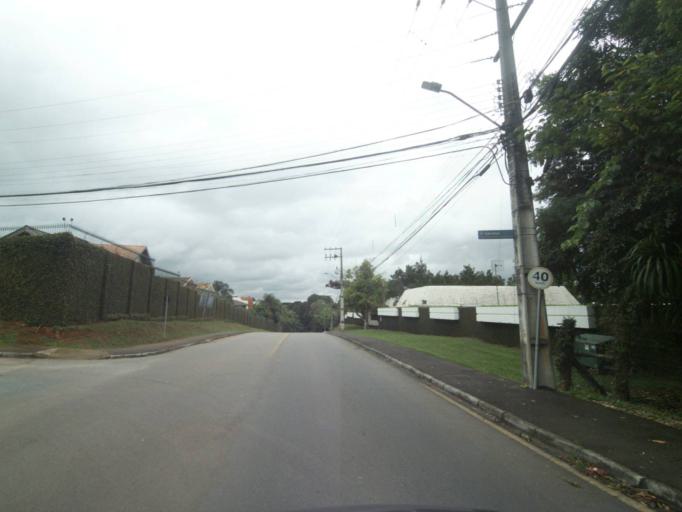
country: BR
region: Parana
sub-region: Curitiba
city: Curitiba
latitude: -25.4534
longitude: -49.3323
